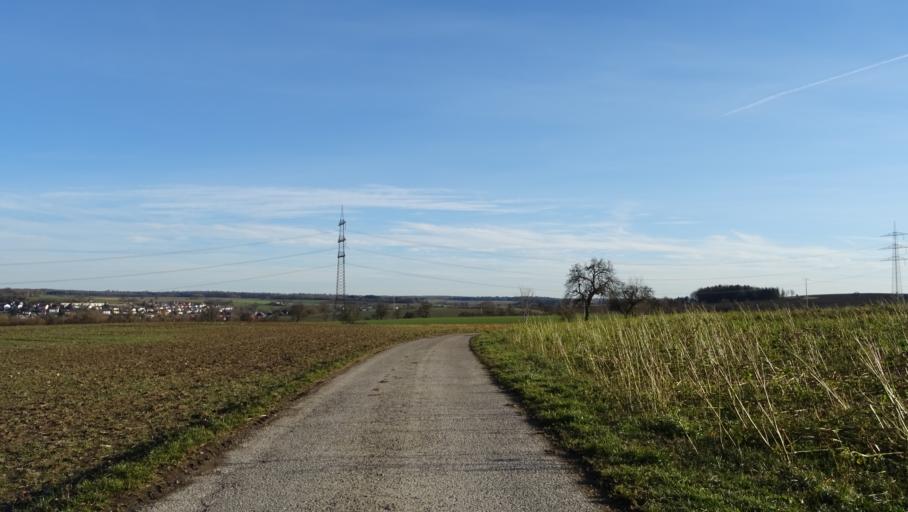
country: DE
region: Baden-Wuerttemberg
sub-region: Karlsruhe Region
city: Limbach
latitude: 49.4188
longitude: 9.2634
